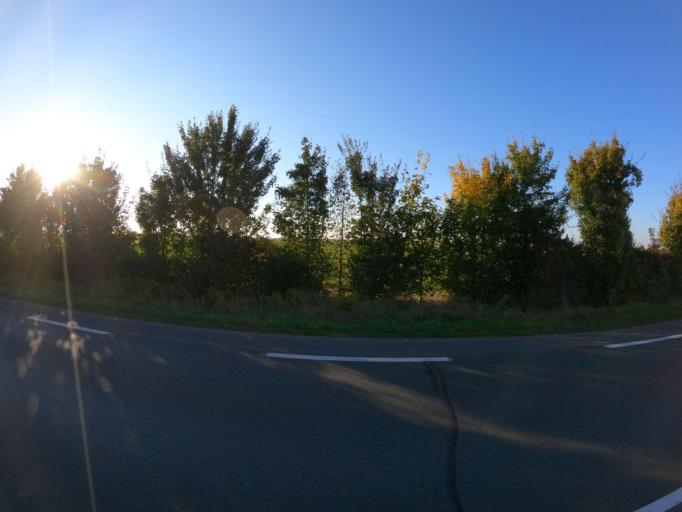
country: FR
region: Pays de la Loire
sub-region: Departement de la Vendee
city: Sainte-Gemme-la-Plaine
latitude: 46.5138
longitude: -1.0905
